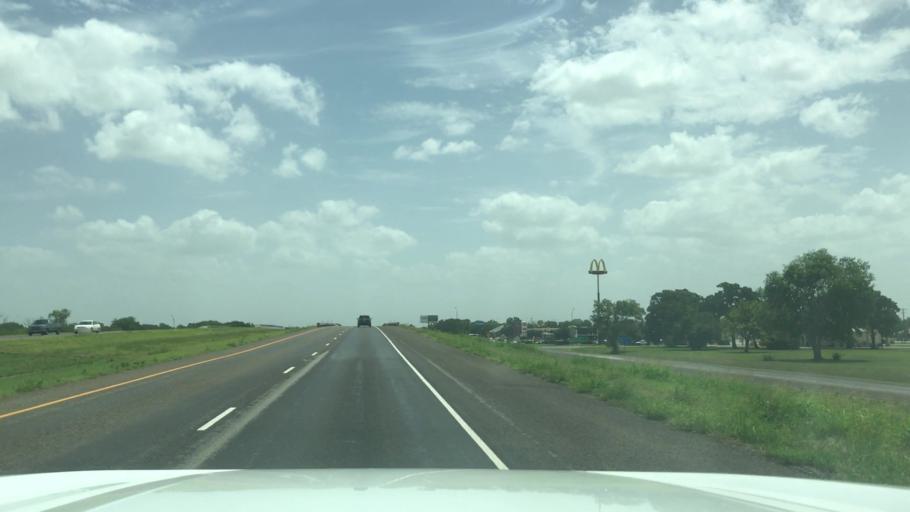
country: US
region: Texas
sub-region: Falls County
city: Marlin
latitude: 31.3087
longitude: -96.8748
